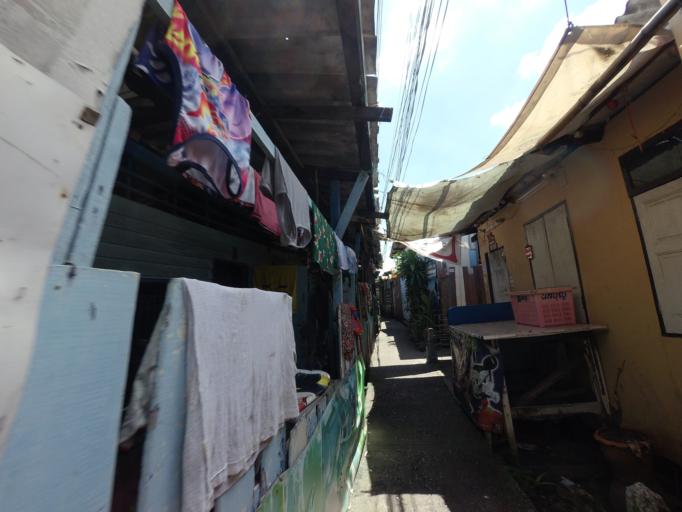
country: TH
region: Bangkok
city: Lat Phrao
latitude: 13.8010
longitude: 100.5887
